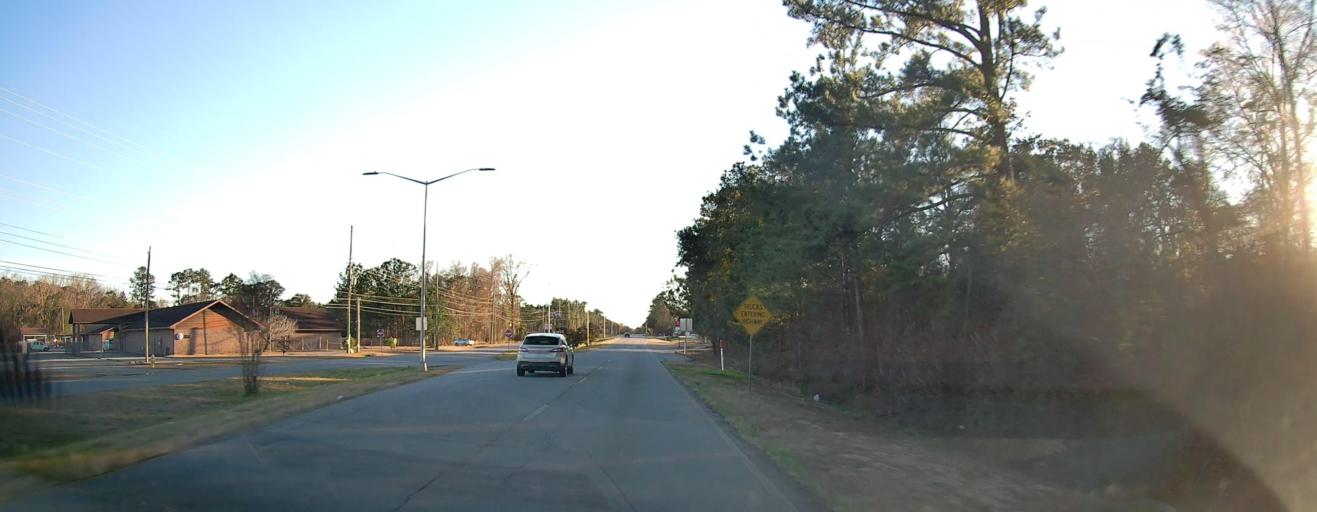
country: US
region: Georgia
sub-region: Dougherty County
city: Albany
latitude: 31.5700
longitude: -84.2220
